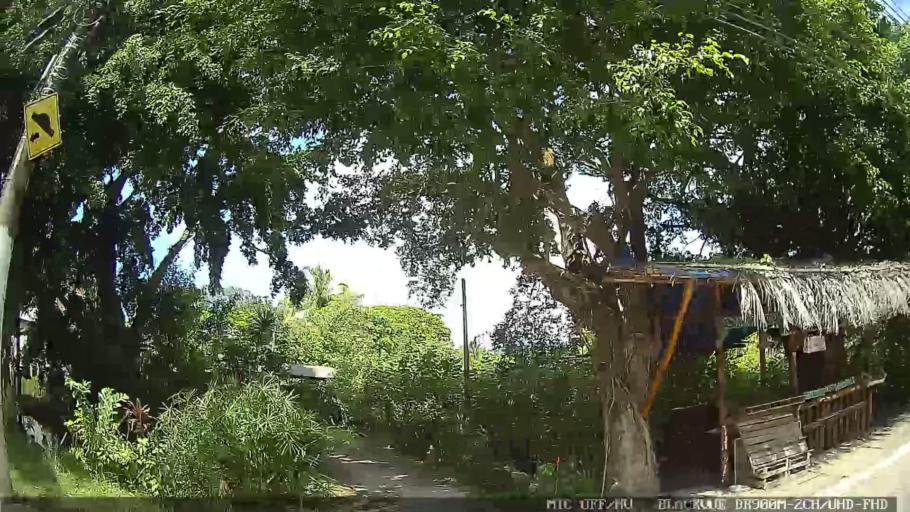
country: BR
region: Sao Paulo
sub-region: Peruibe
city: Peruibe
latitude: -24.3057
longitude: -47.0139
